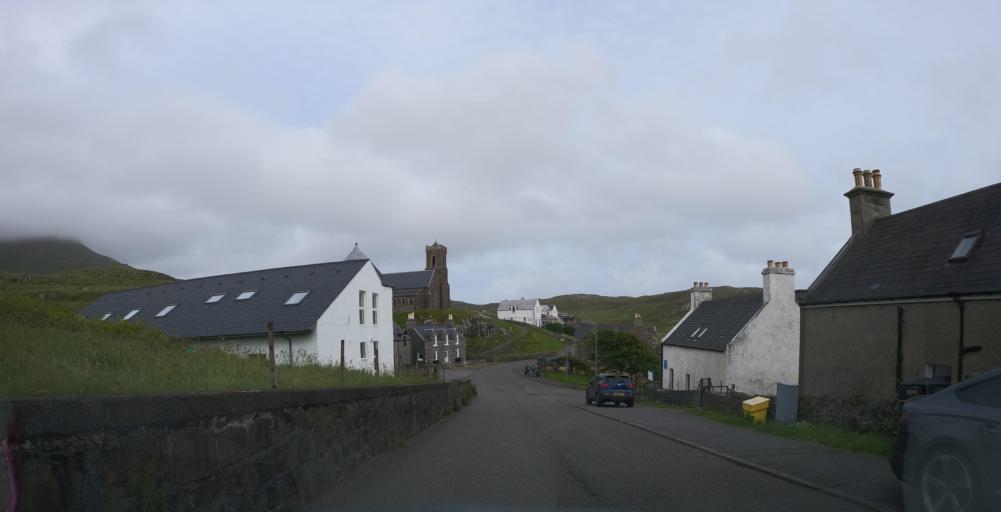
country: GB
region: Scotland
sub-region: Eilean Siar
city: Barra
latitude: 56.9551
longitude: -7.4866
